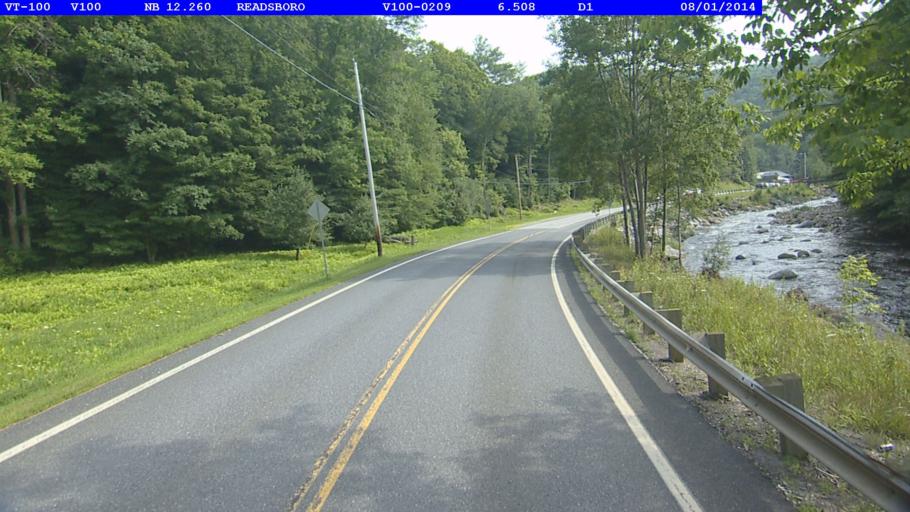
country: US
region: Massachusetts
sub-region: Franklin County
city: Charlemont
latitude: 42.7774
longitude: -72.9516
